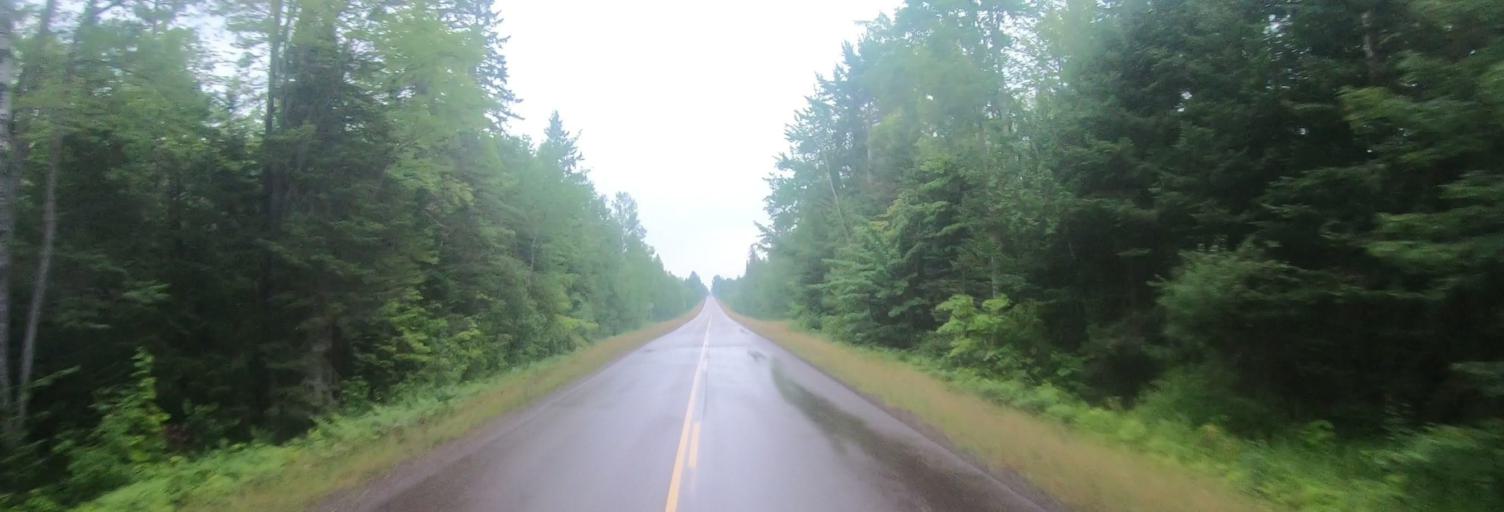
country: US
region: Michigan
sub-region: Keweenaw County
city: Eagle River
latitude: 47.2775
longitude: -88.2668
